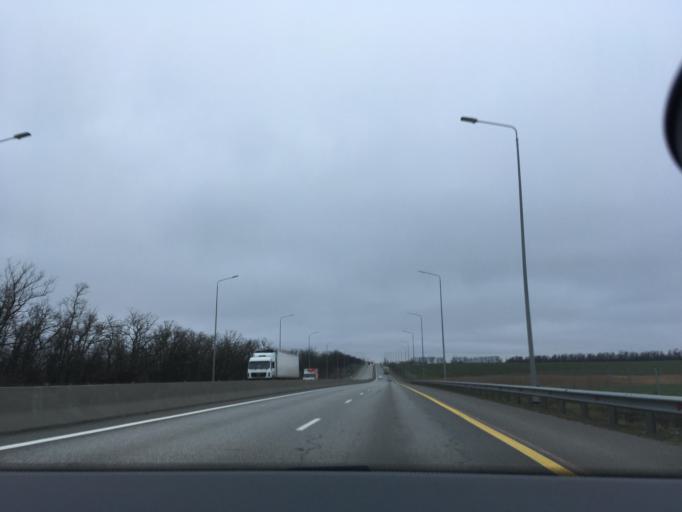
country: RU
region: Krasnodarskiy
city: Krasnoye
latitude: 46.8001
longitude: 39.6682
